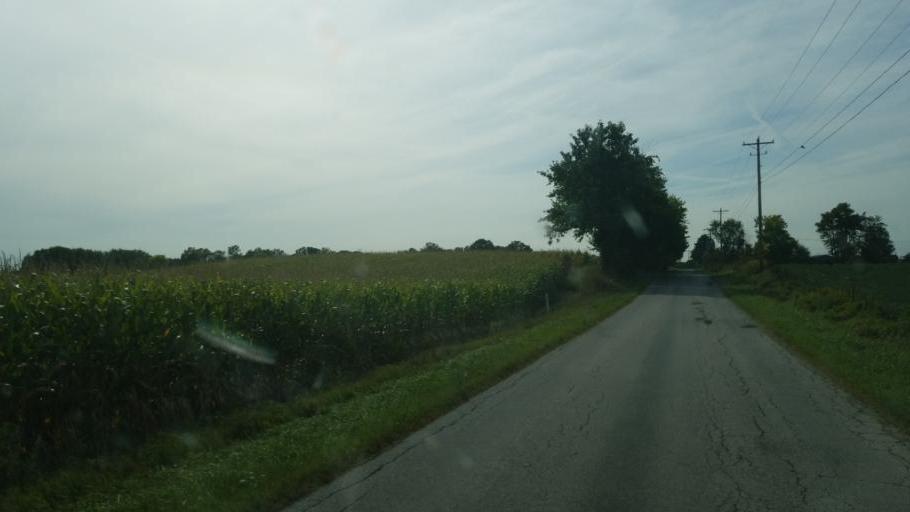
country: US
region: Ohio
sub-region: Knox County
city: Centerburg
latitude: 40.4038
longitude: -82.6486
